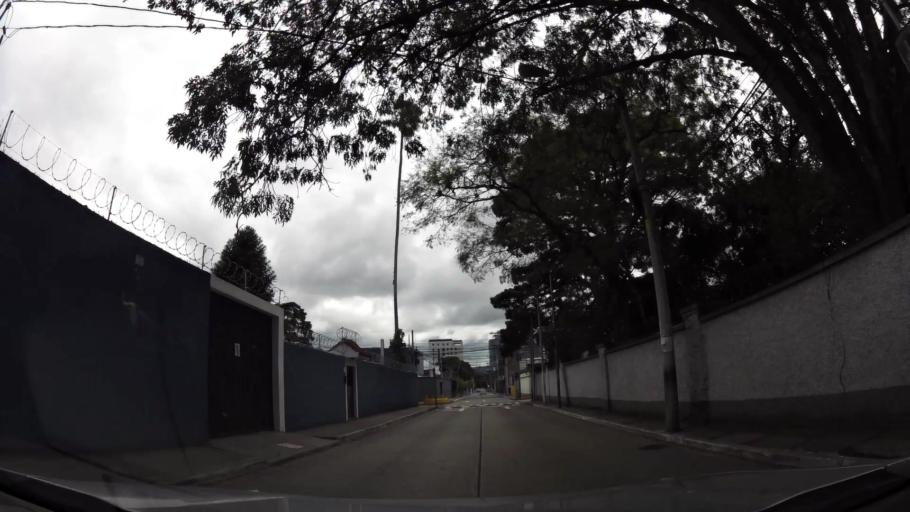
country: GT
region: Guatemala
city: Guatemala City
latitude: 14.6047
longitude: -90.5142
